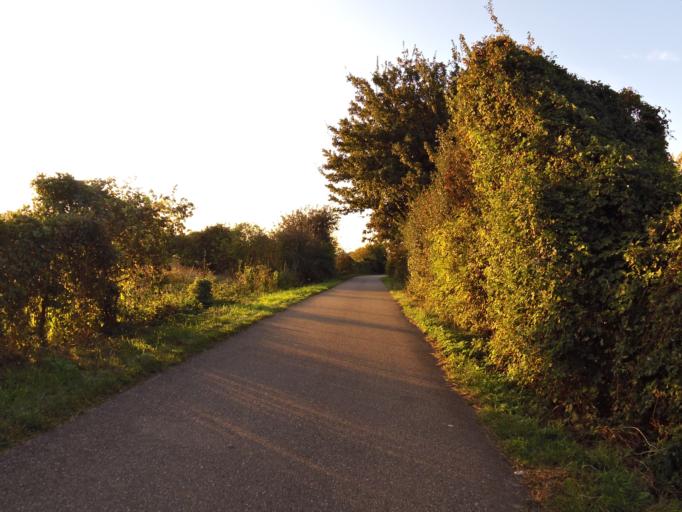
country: NL
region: North Brabant
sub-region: Gemeente Boxmeer
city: Boxmeer
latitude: 51.6464
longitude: 5.9689
